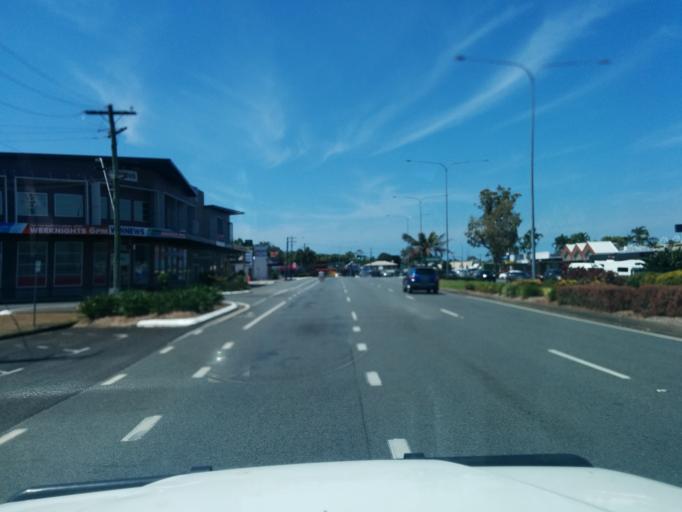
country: AU
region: Queensland
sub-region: Cairns
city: Woree
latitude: -16.9445
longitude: 145.7382
